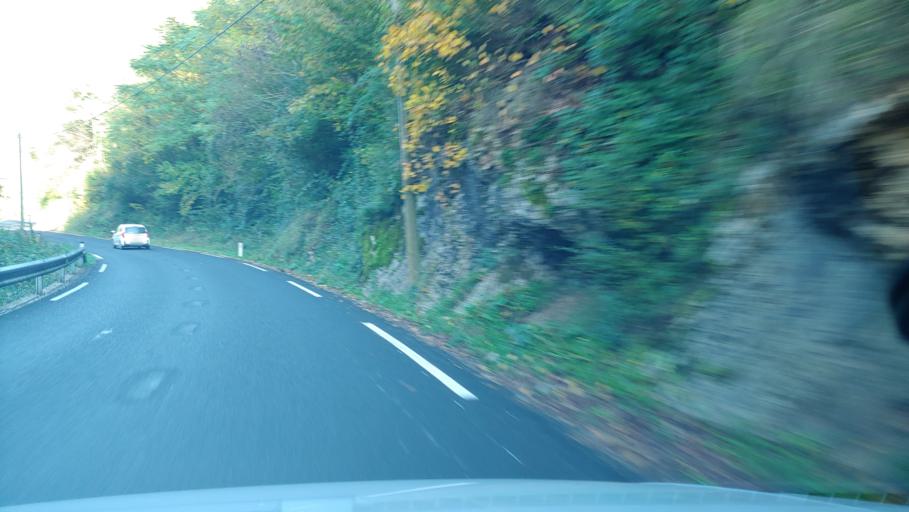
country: SI
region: Ajdovscina
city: Ajdovscina
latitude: 45.8096
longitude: 13.8761
